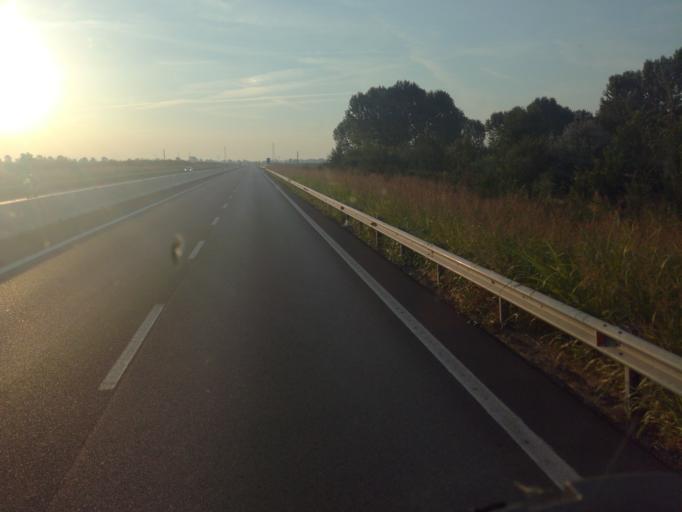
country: IT
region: Lombardy
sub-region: Provincia di Cremona
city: Nosadello
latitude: 45.3915
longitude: 9.5093
